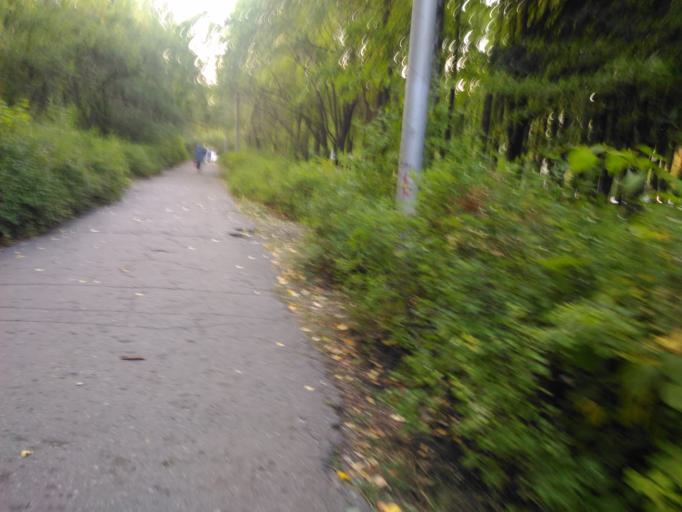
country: RU
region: Ulyanovsk
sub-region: Ulyanovskiy Rayon
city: Ulyanovsk
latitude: 54.3038
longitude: 48.3246
